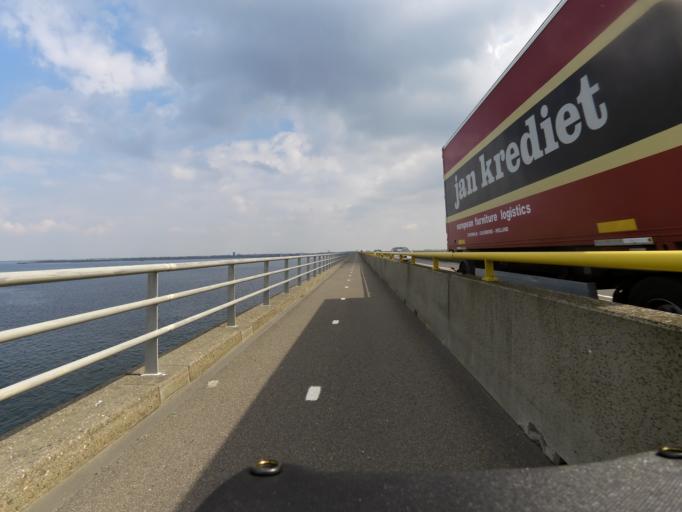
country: NL
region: Zeeland
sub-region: Gemeente Goes
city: Goes
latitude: 51.6142
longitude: 3.8939
